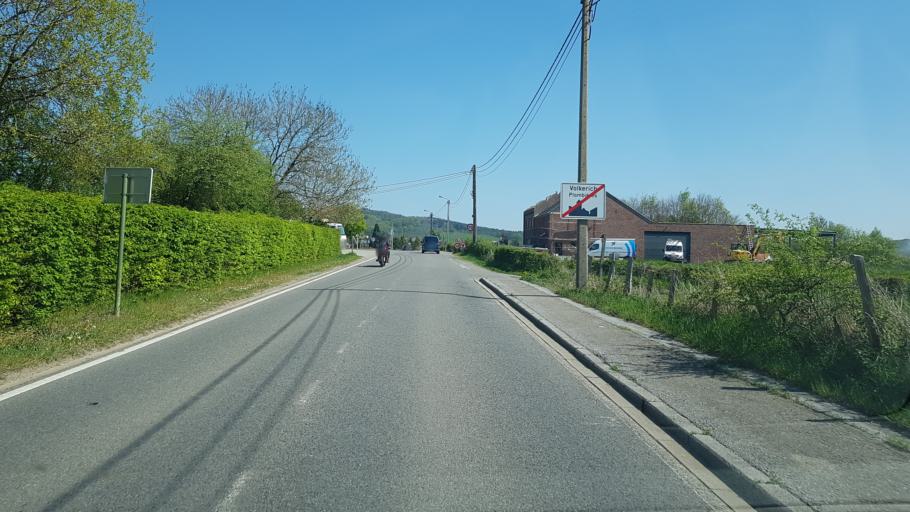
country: BE
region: Wallonia
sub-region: Province de Liege
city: Plombieres
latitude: 50.7432
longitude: 5.9830
